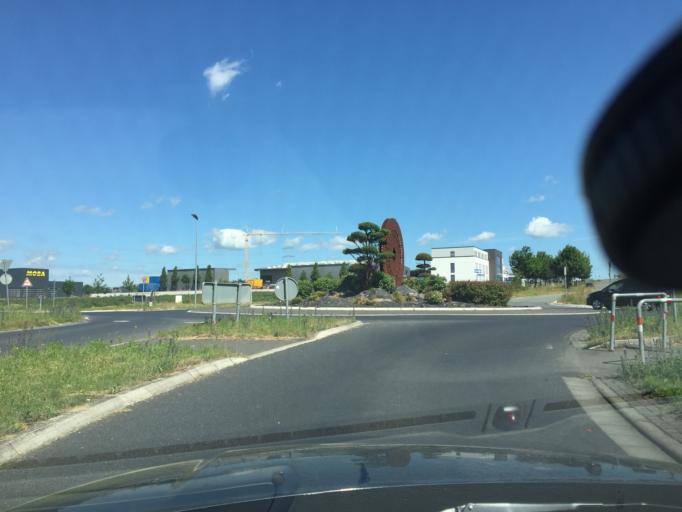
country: DE
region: Hesse
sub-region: Regierungsbezirk Giessen
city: Dehrn
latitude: 50.4095
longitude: 8.0723
